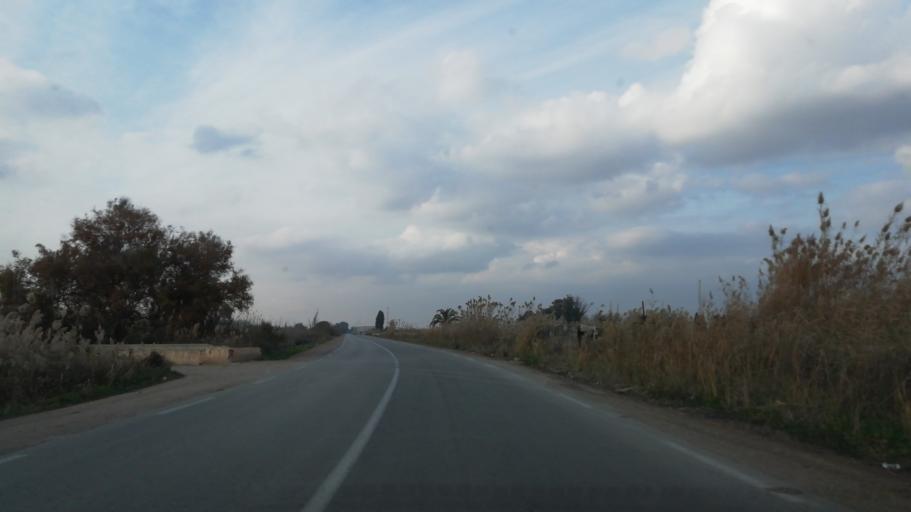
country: DZ
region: Mascara
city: Sig
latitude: 35.6495
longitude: 0.0237
